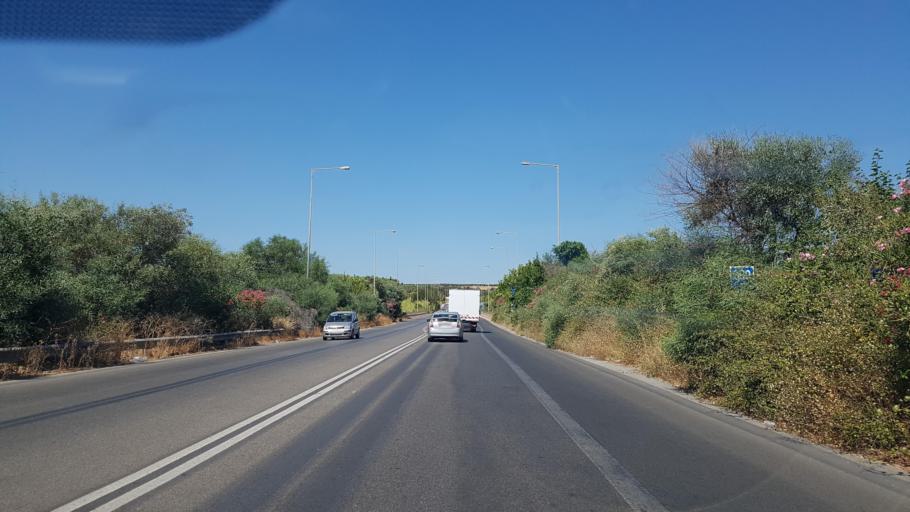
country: GR
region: Crete
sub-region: Nomos Chanias
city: Gerani
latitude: 35.5119
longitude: 23.8966
